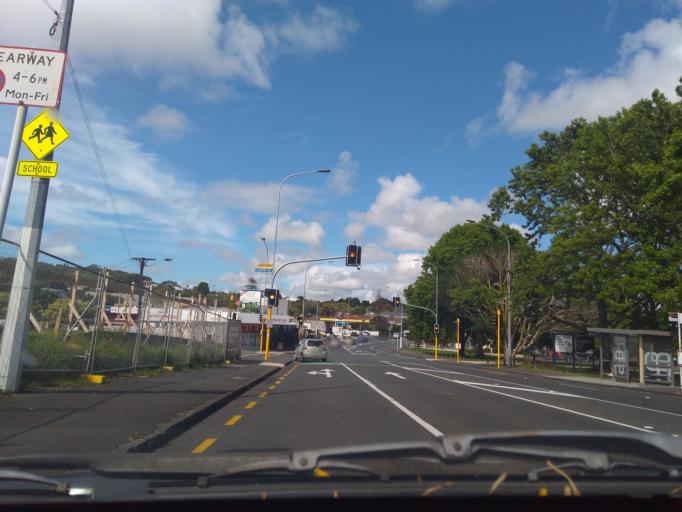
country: NZ
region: Auckland
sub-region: Auckland
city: Auckland
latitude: -36.8795
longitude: 174.7266
